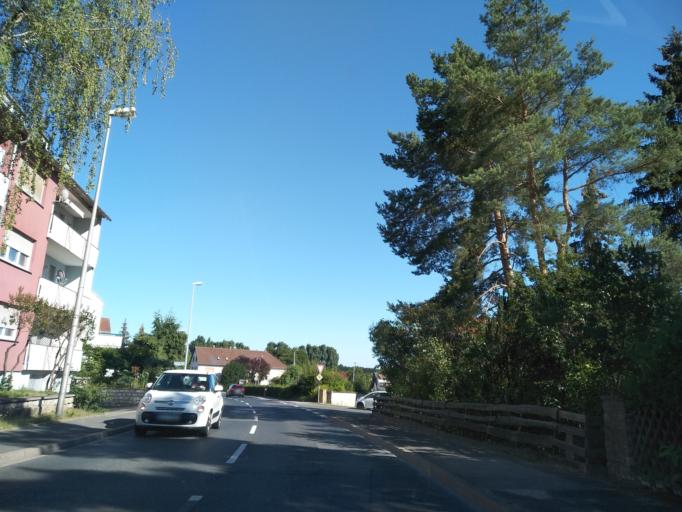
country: DE
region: Bavaria
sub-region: Regierungsbezirk Mittelfranken
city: Hessdorf
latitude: 49.6300
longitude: 10.9355
